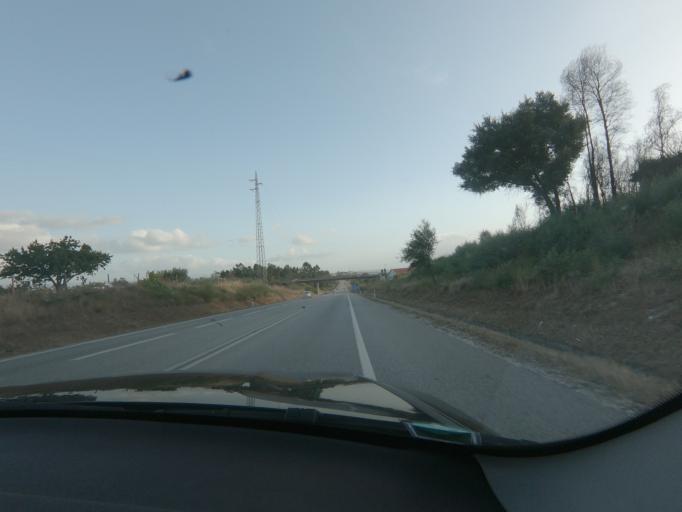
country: PT
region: Viseu
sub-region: Santa Comba Dao
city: Santa Comba Dao
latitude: 40.3693
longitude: -8.1296
